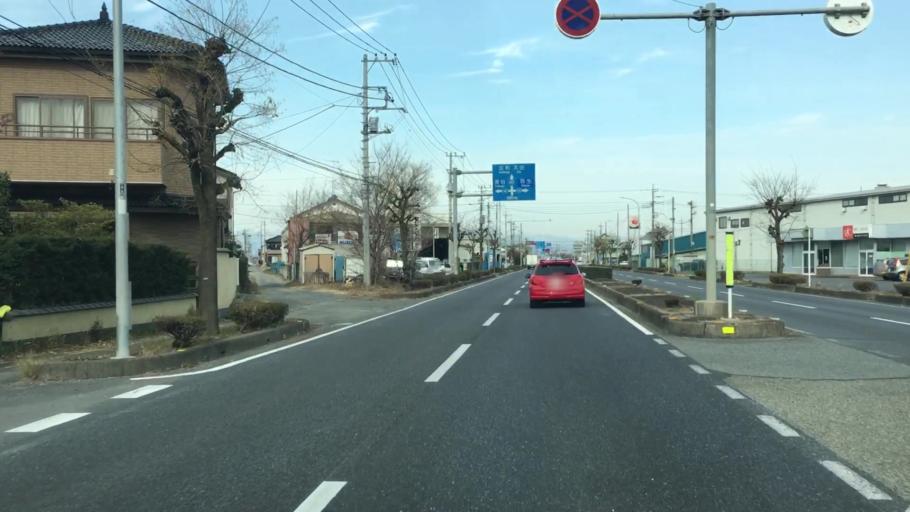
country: JP
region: Saitama
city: Menuma
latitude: 36.2246
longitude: 139.3695
